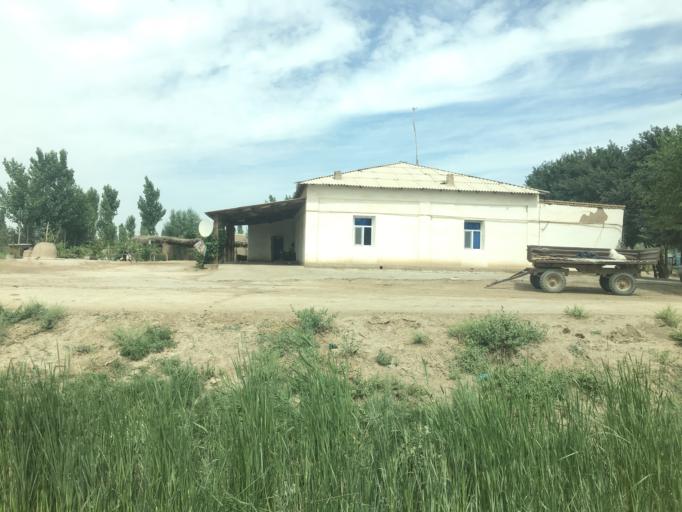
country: TM
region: Dasoguz
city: Tagta
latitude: 41.5989
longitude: 59.8557
